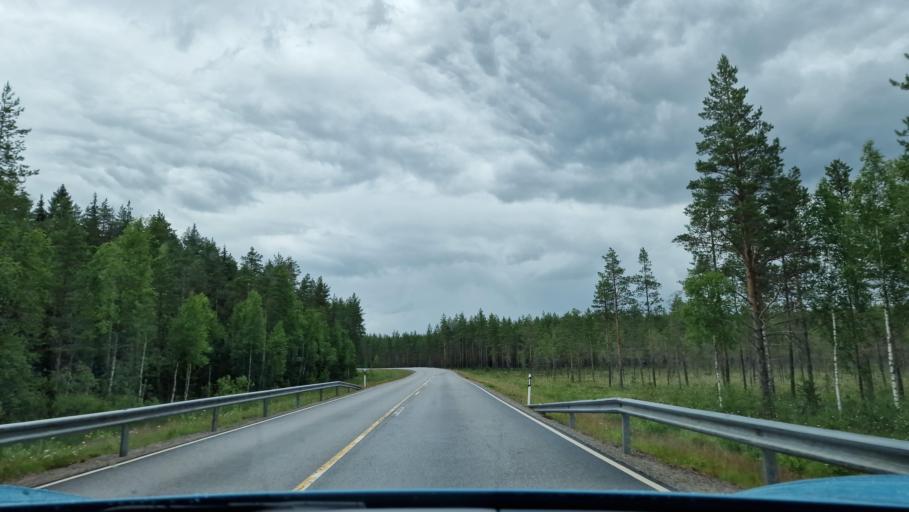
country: FI
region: Central Finland
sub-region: Saarijaervi-Viitasaari
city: Pylkoenmaeki
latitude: 62.6190
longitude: 24.5809
